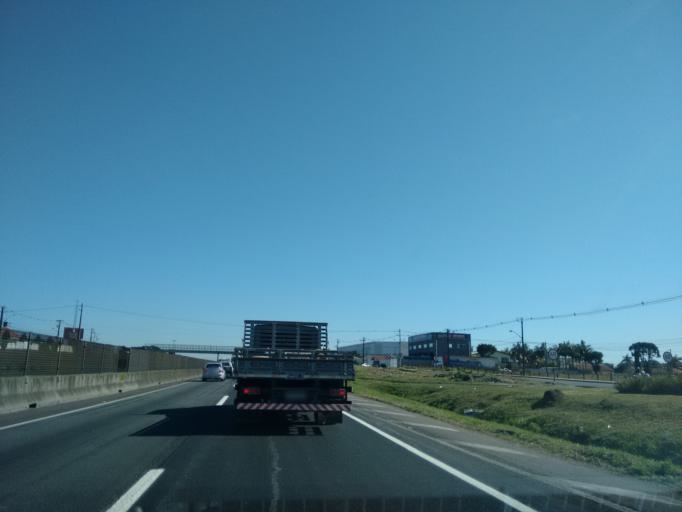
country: BR
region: Parana
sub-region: Sao Jose Dos Pinhais
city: Sao Jose dos Pinhais
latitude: -25.5483
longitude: -49.2860
